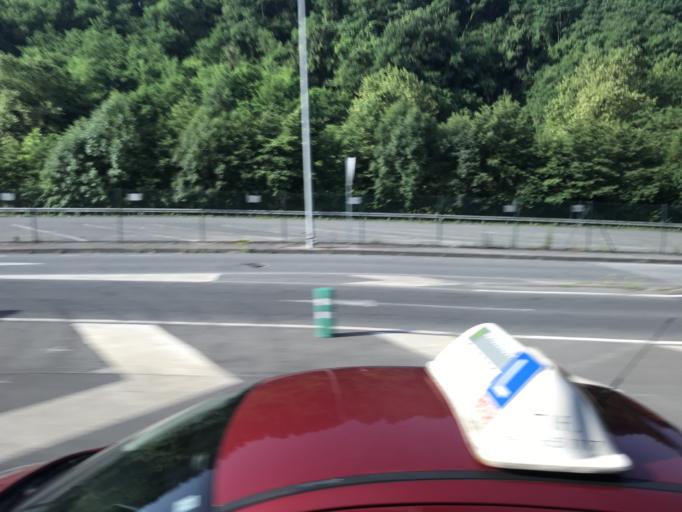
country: ES
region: Basque Country
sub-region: Provincia de Guipuzcoa
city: Beasain
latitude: 43.0457
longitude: -2.2054
